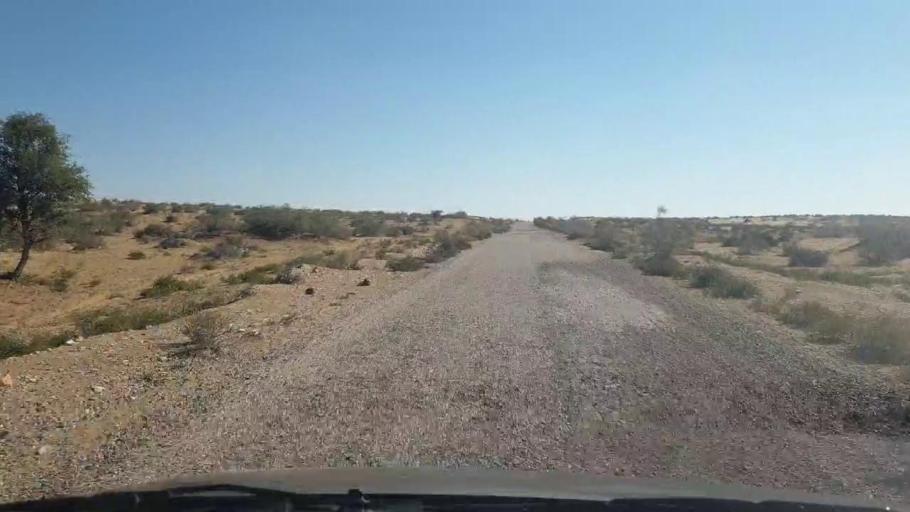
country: PK
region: Sindh
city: Bozdar
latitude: 27.0061
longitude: 68.8025
